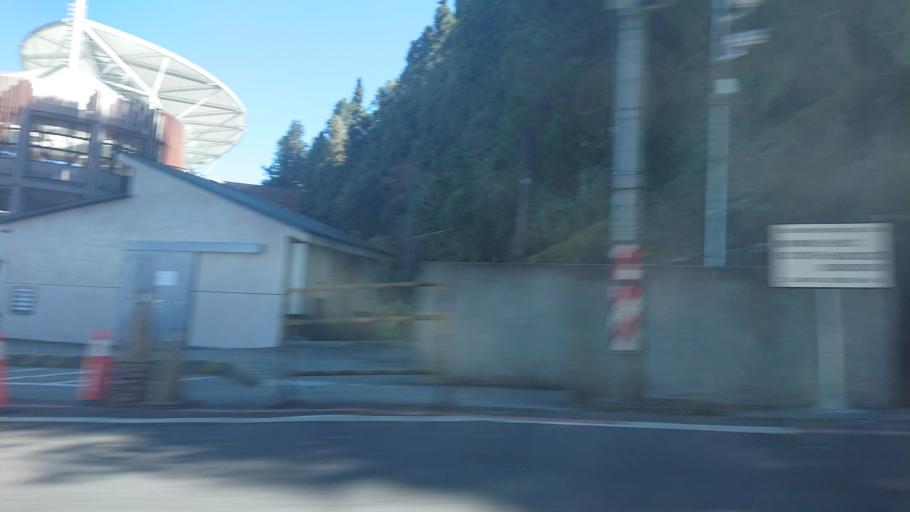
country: TW
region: Taiwan
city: Lugu
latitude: 23.5079
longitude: 120.8013
